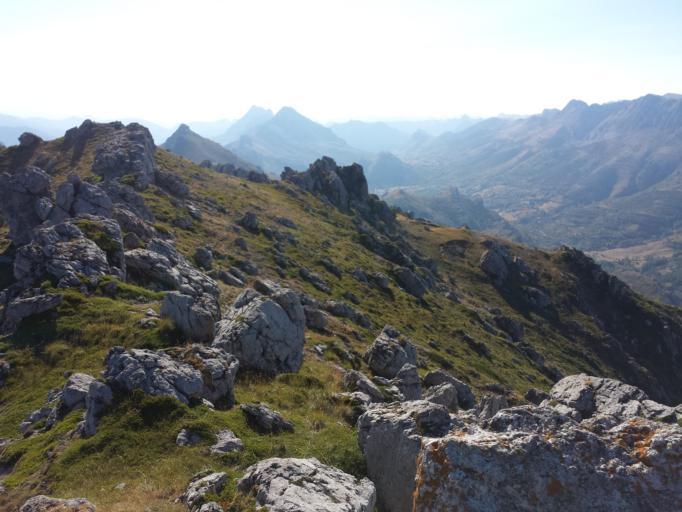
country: ES
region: Castille and Leon
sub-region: Provincia de Leon
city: Carmenes
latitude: 42.9634
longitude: -5.5375
